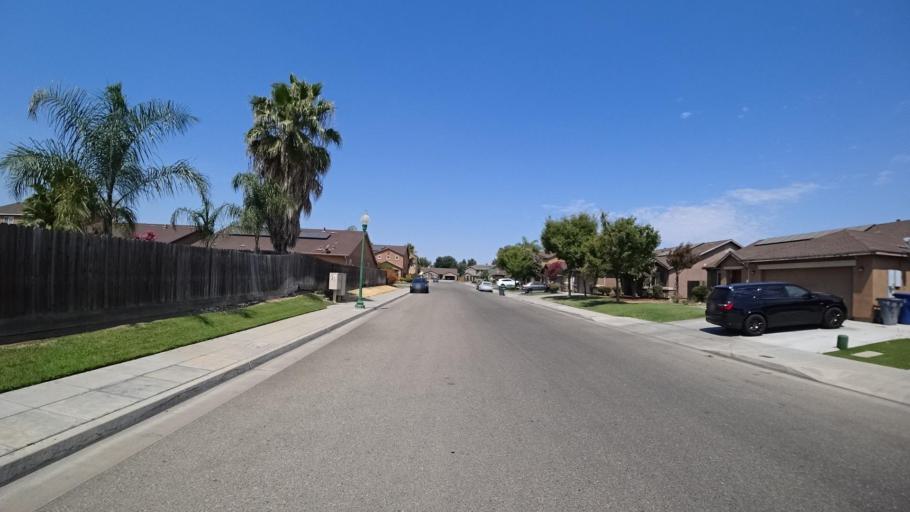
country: US
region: California
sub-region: Fresno County
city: Sunnyside
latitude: 36.7390
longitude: -119.6899
